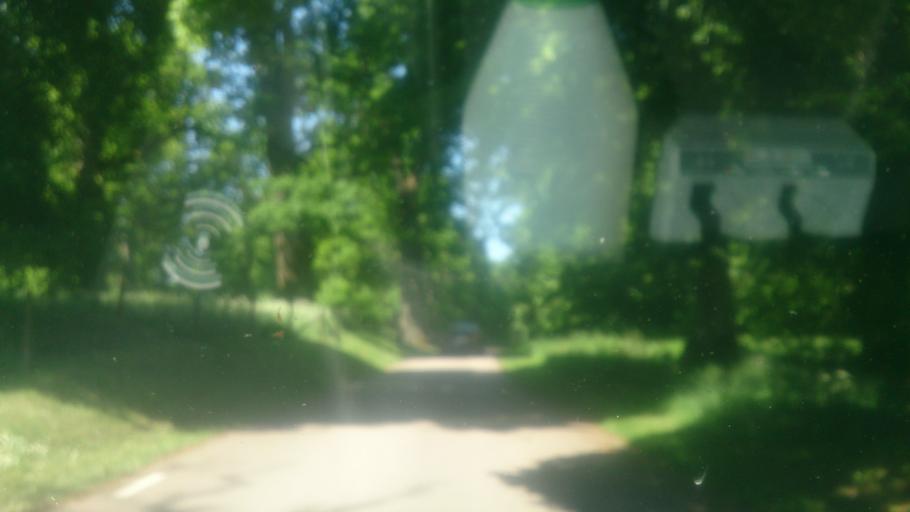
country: SE
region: OEstergoetland
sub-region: Atvidabergs Kommun
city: Atvidaberg
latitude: 58.1840
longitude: 15.9985
